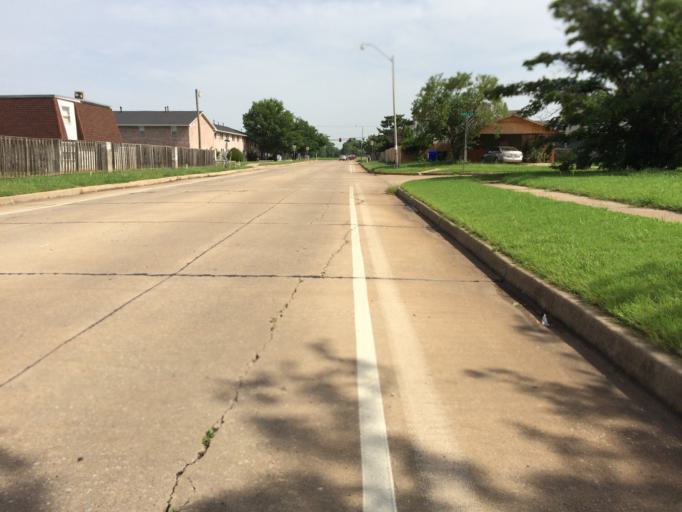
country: US
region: Oklahoma
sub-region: Cleveland County
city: Hall Park
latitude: 35.2167
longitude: -97.4164
